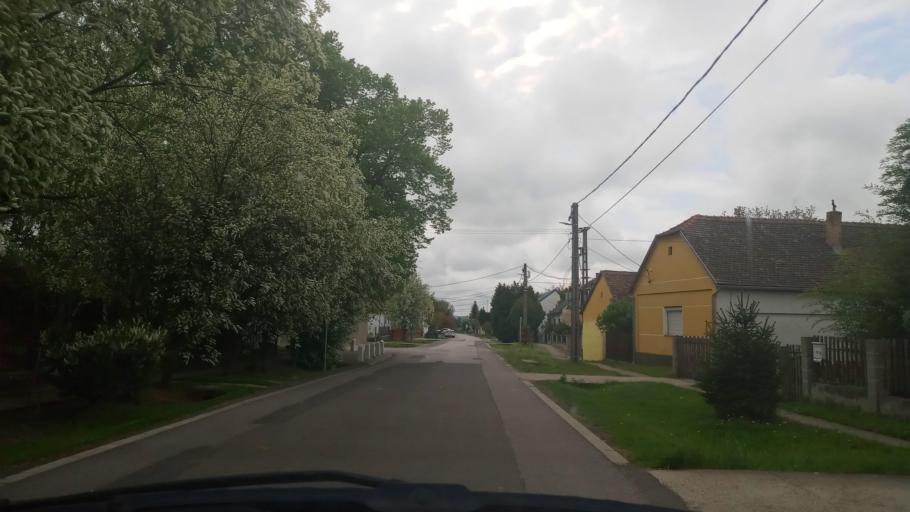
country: HU
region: Baranya
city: Kozarmisleny
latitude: 46.0001
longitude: 18.3753
